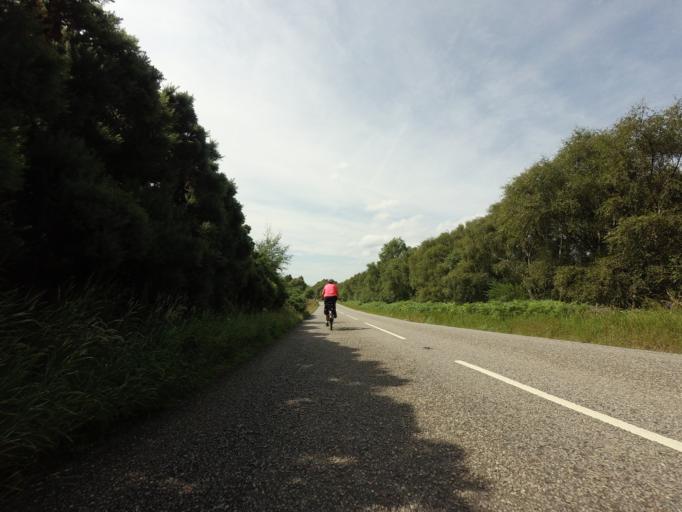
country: GB
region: Scotland
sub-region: Highland
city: Alness
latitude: 57.8580
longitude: -4.2331
